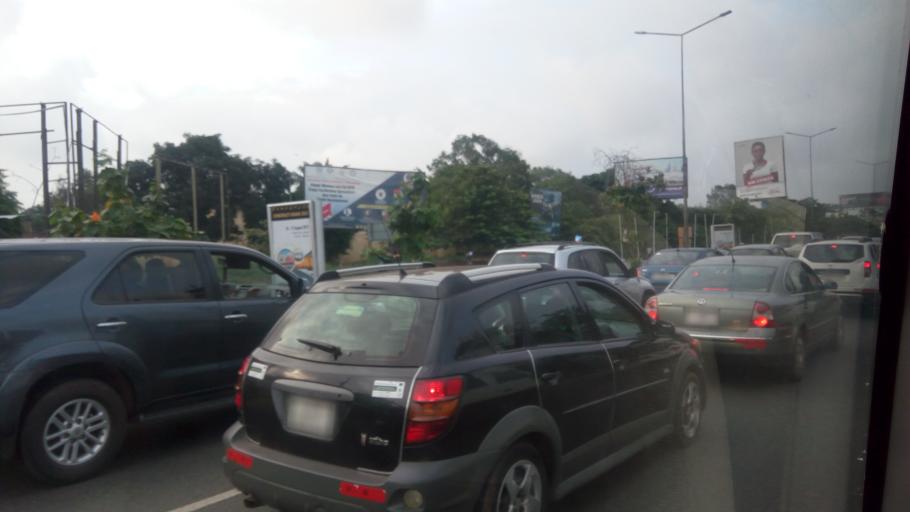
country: GH
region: Greater Accra
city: Accra
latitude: 5.5996
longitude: -0.1783
